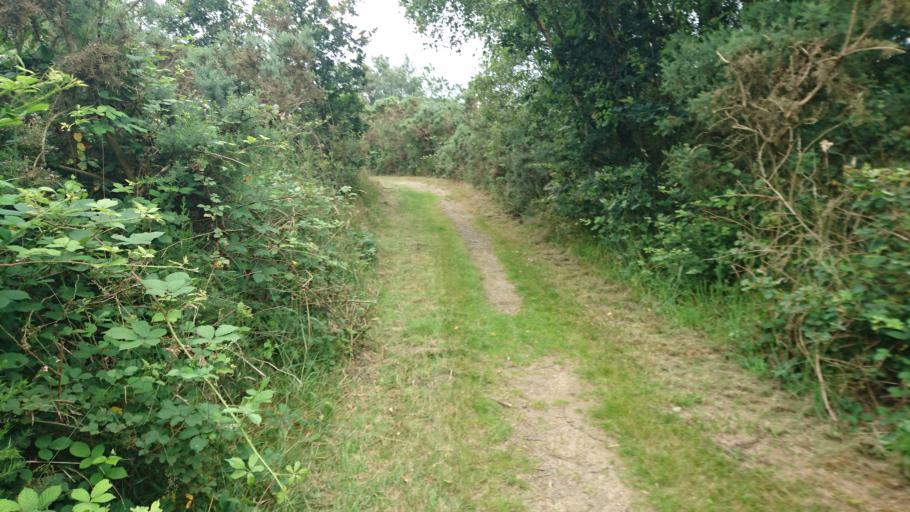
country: FR
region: Brittany
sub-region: Departement d'Ille-et-Vilaine
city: Saint-Just
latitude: 47.7651
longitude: -1.9855
